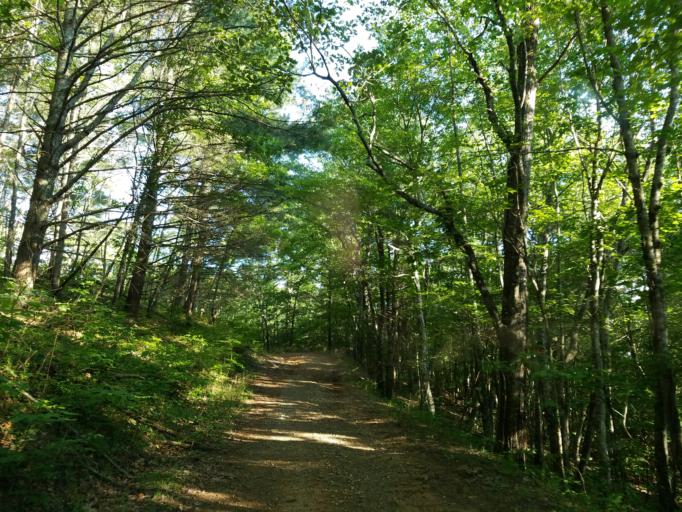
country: US
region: Georgia
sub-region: Fannin County
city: Blue Ridge
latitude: 34.8070
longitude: -84.1665
